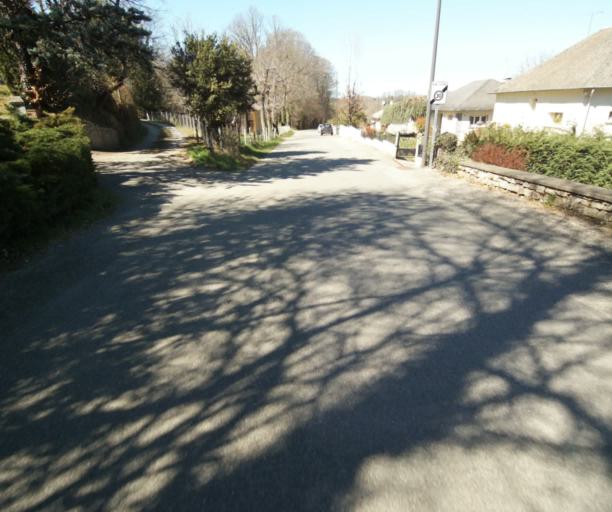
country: FR
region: Limousin
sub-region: Departement de la Correze
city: Seilhac
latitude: 45.3684
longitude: 1.7122
